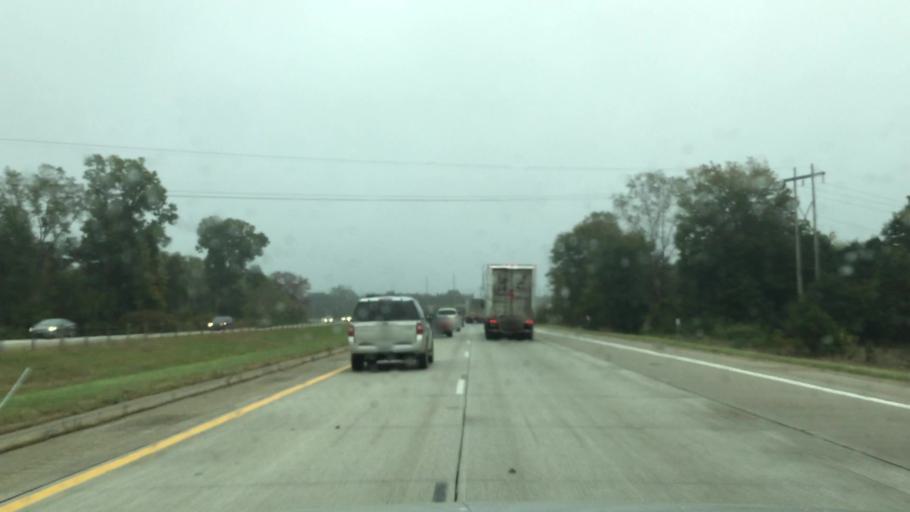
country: US
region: Michigan
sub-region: Van Buren County
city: Paw Paw
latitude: 42.2062
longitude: -85.8874
